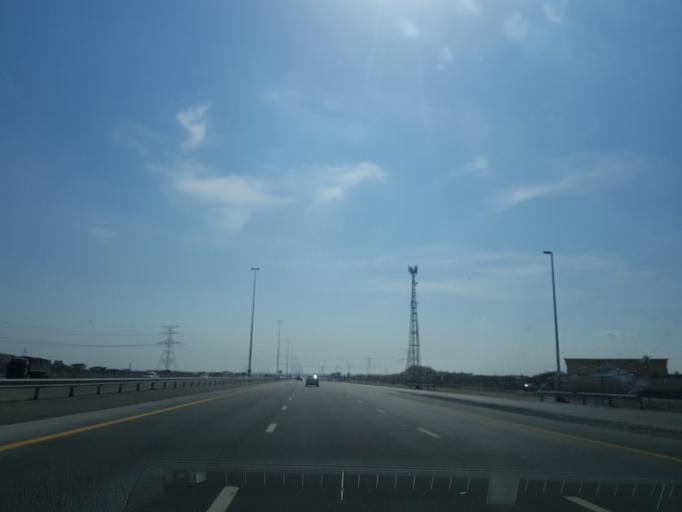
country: AE
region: Ra's al Khaymah
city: Ras al-Khaimah
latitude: 25.7725
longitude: 56.0276
